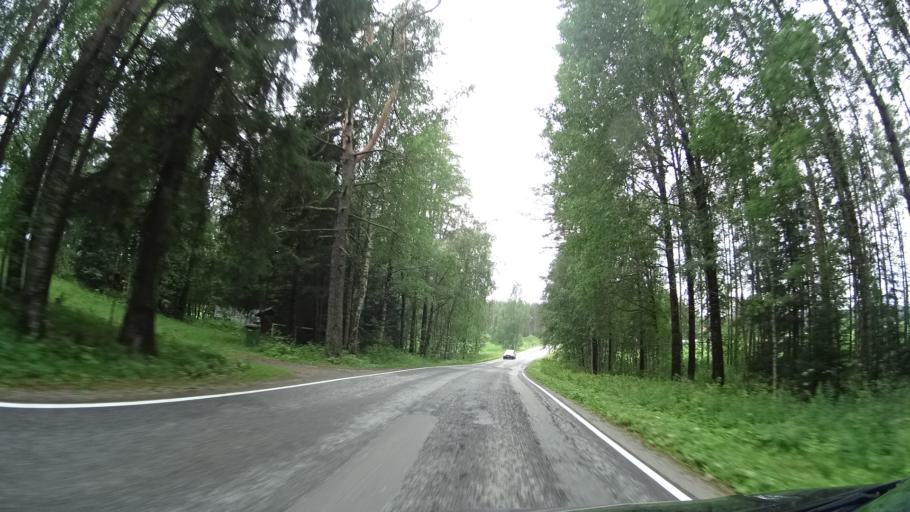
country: FI
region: Southern Savonia
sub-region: Savonlinna
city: Punkaharju
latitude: 61.7470
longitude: 29.4998
